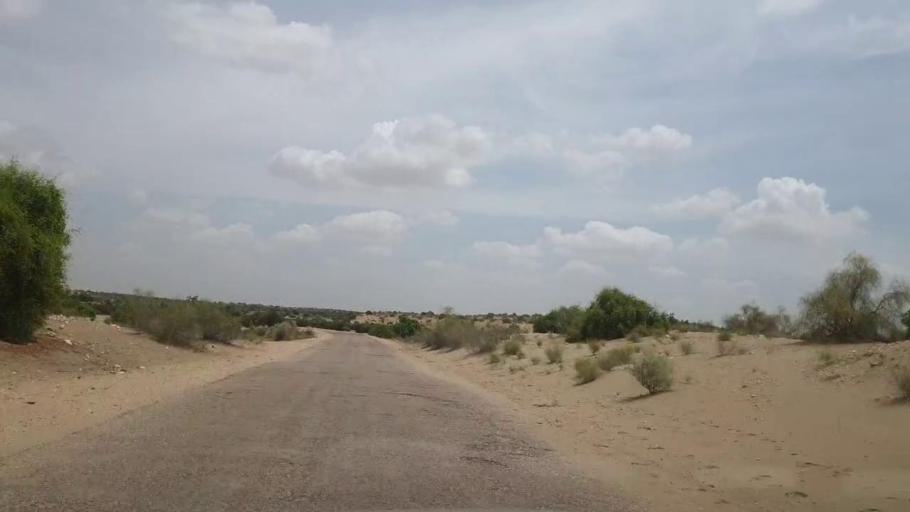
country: PK
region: Sindh
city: Kot Diji
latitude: 27.1845
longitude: 69.1714
